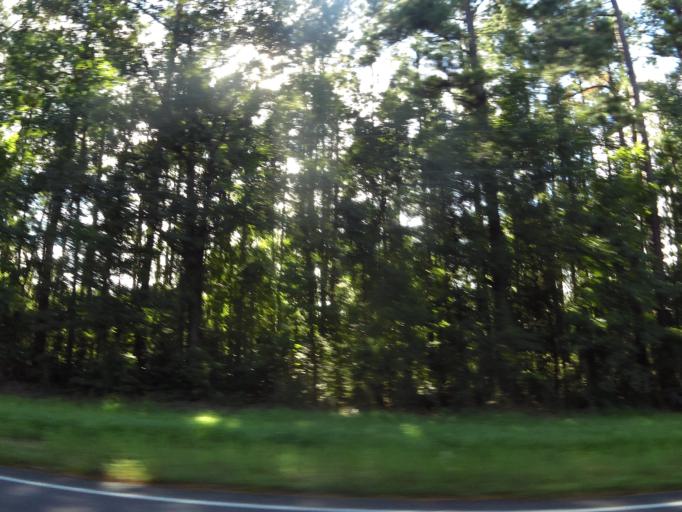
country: US
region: Georgia
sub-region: Camden County
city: Woodbine
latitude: 31.0481
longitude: -81.7295
